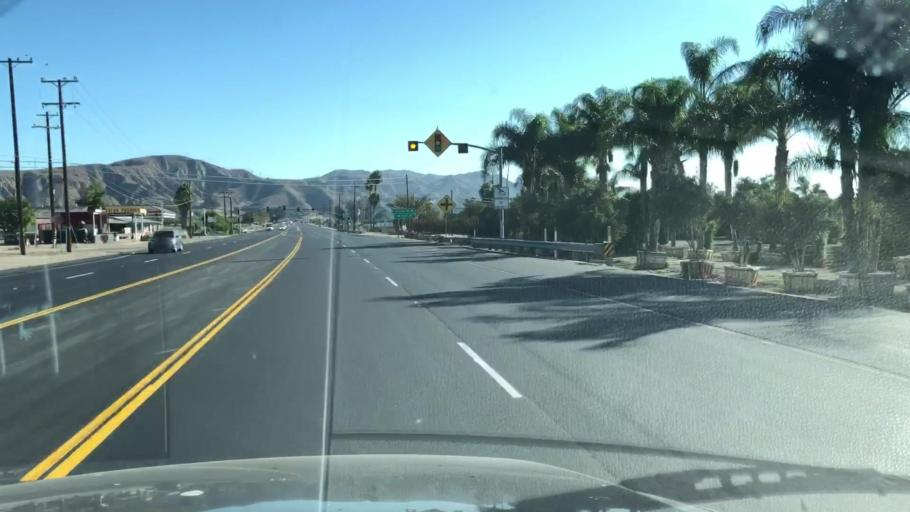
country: US
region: California
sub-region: Ventura County
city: Piru
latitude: 34.4039
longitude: -118.7968
